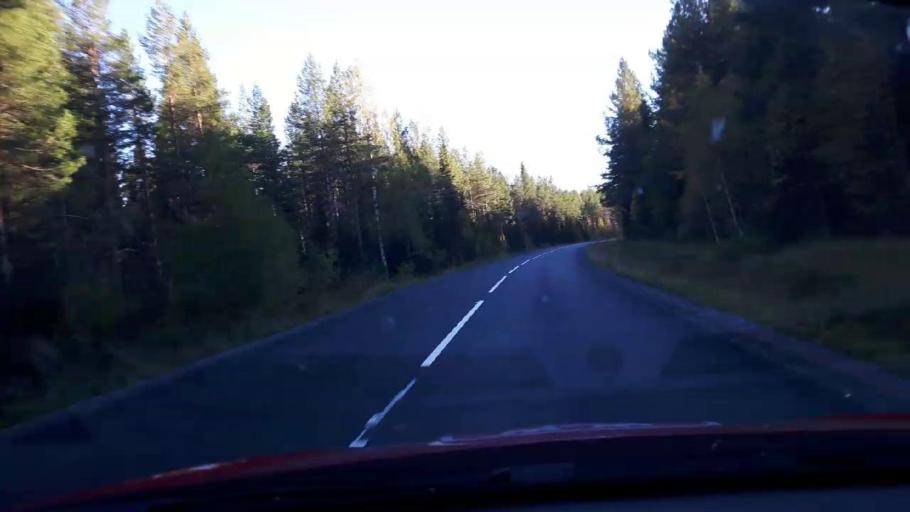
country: SE
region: Jaemtland
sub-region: OEstersunds Kommun
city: Lit
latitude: 63.4706
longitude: 14.8772
